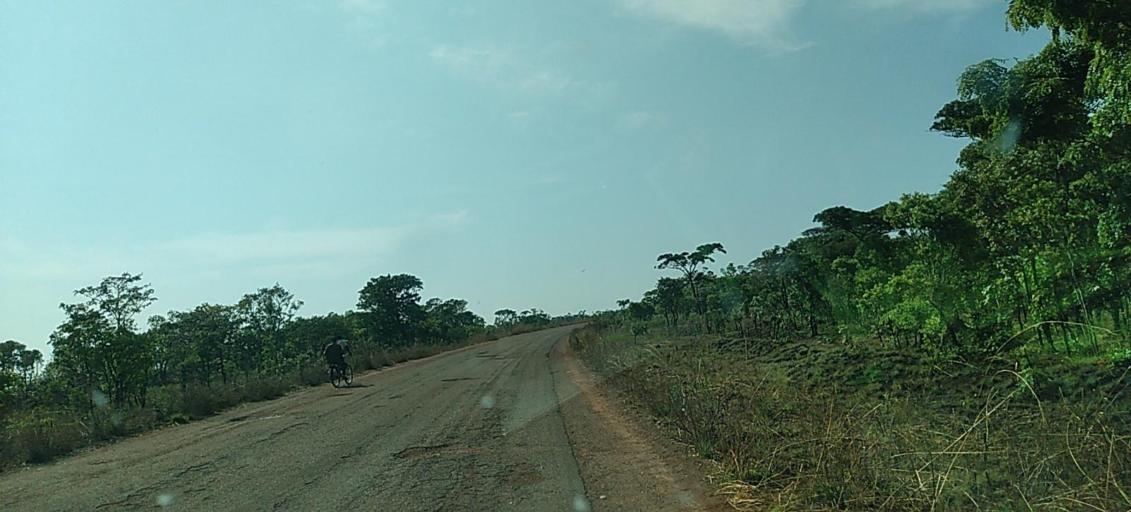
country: ZM
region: North-Western
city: Mwinilunga
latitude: -11.7769
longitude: 25.0197
